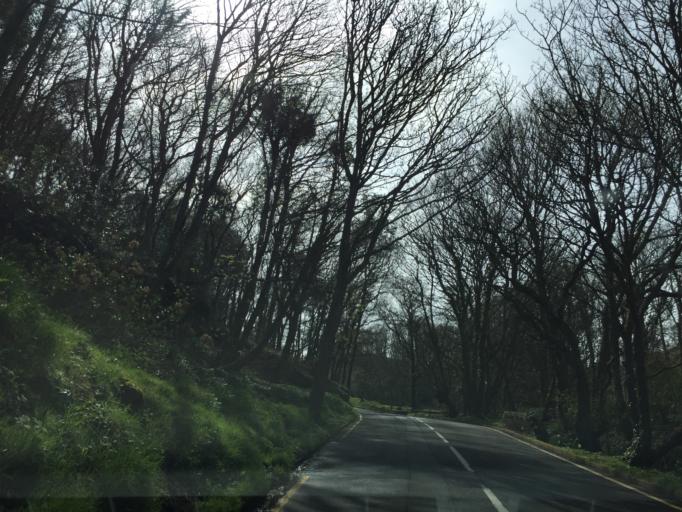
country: JE
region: St Helier
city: Saint Helier
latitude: 49.2444
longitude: -2.2024
